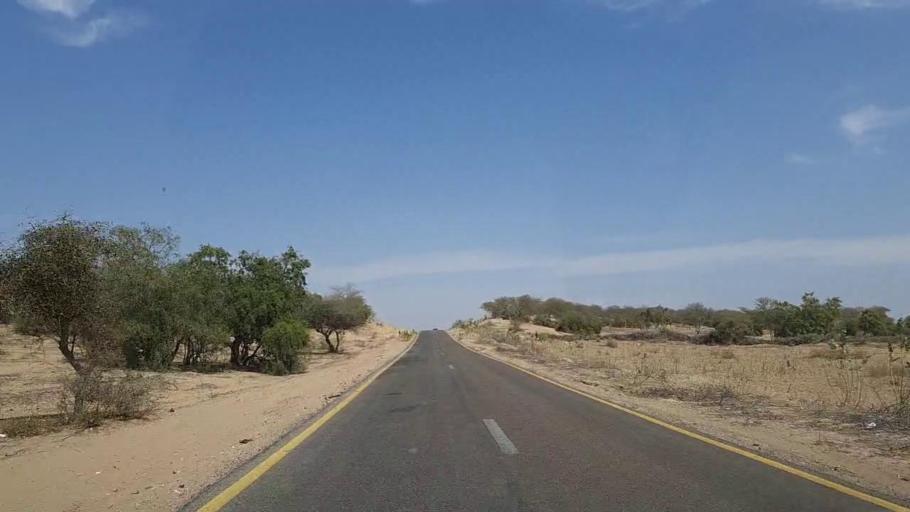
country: PK
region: Sindh
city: Mithi
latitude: 24.8580
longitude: 69.8412
